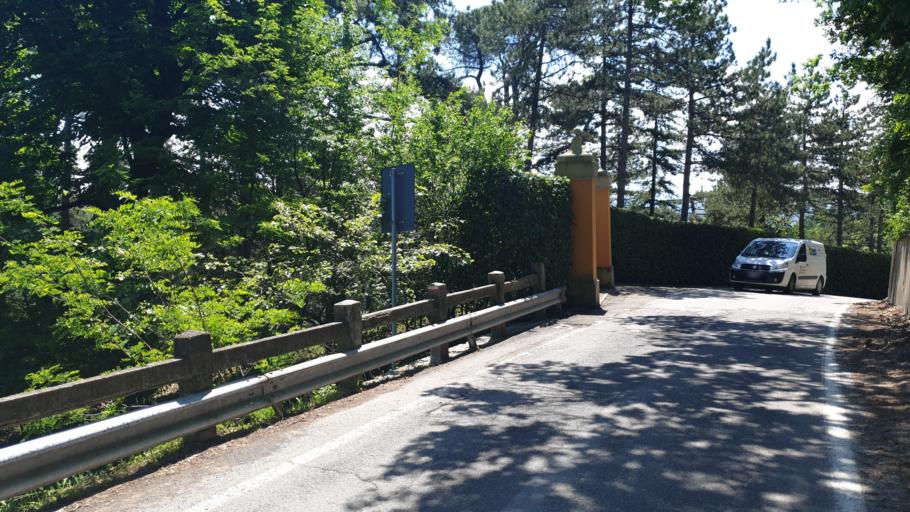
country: IT
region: Emilia-Romagna
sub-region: Provincia di Bologna
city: Casalecchio di Reno
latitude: 44.4764
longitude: 11.2946
